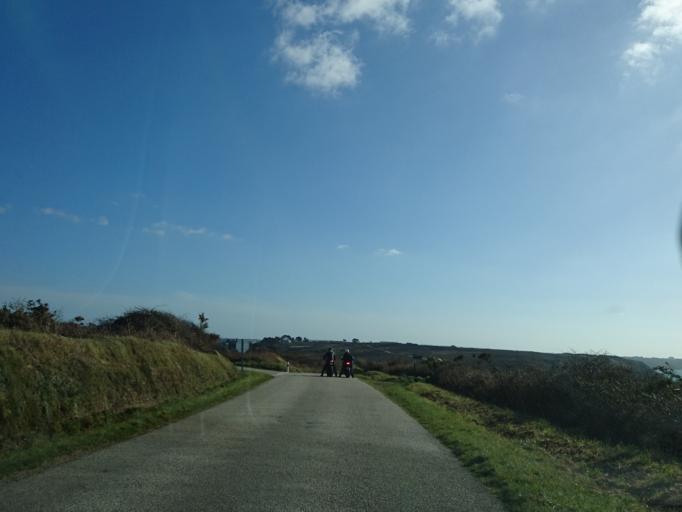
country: FR
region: Brittany
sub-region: Departement du Finistere
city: Roscanvel
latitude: 48.3125
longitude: -4.5708
